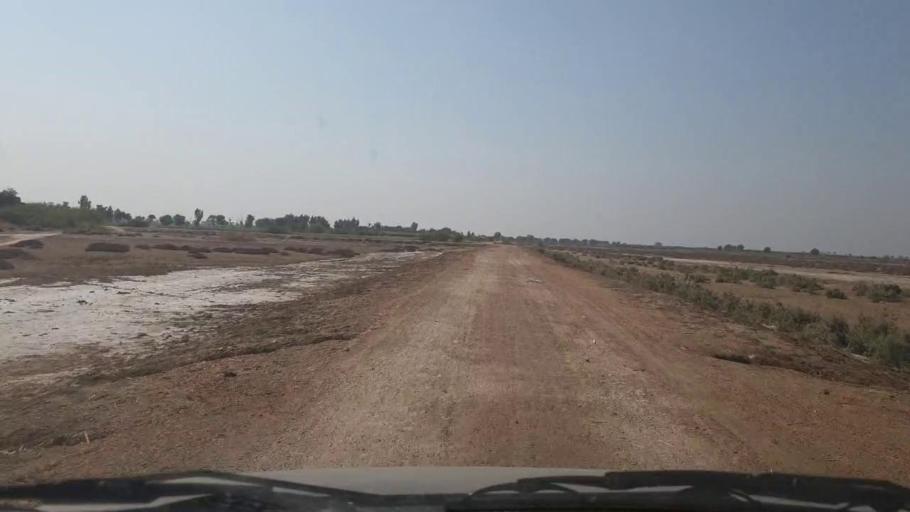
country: PK
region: Sindh
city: Samaro
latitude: 25.2661
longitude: 69.3430
